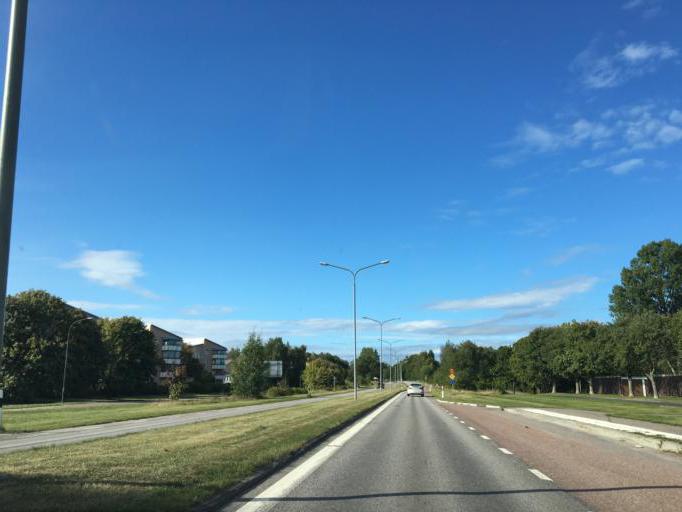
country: SE
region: Soedermanland
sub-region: Nykopings Kommun
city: Nykoping
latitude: 58.7705
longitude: 16.9855
